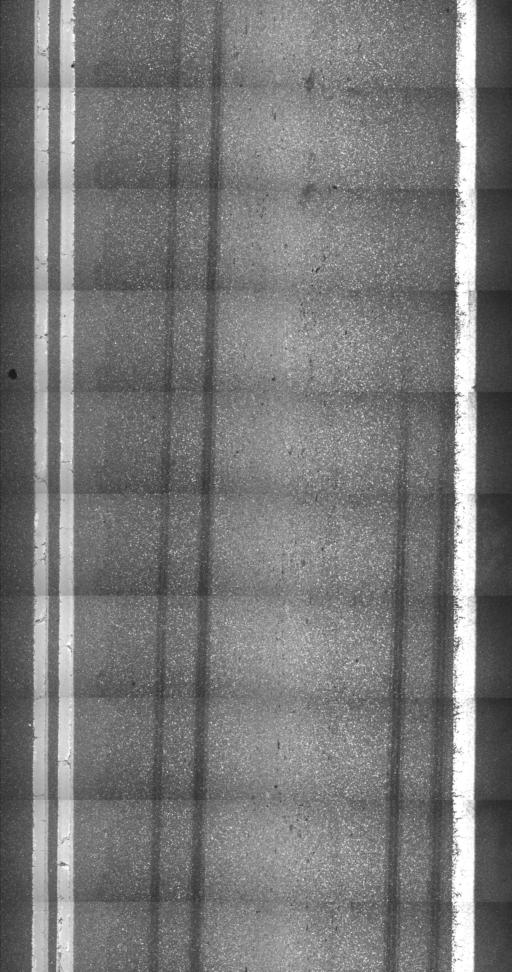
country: US
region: Vermont
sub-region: Windsor County
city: Springfield
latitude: 43.4069
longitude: -72.5056
